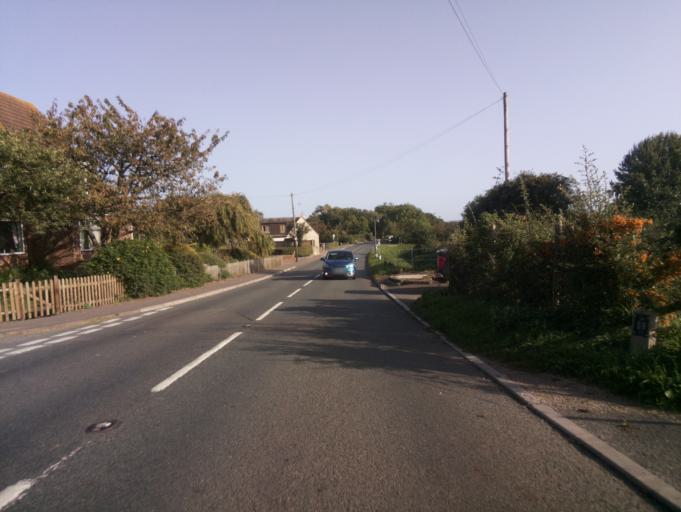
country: GB
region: England
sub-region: Gloucestershire
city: Tewkesbury
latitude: 51.9541
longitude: -2.2375
